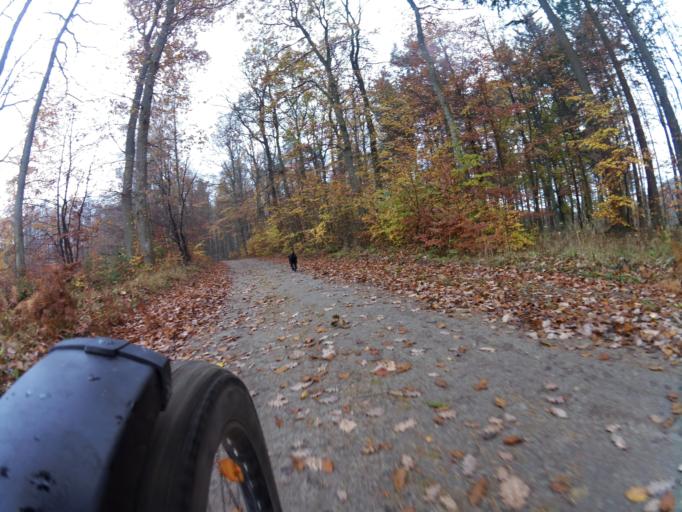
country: PL
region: Pomeranian Voivodeship
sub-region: Powiat pucki
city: Krokowa
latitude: 54.7678
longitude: 18.0952
